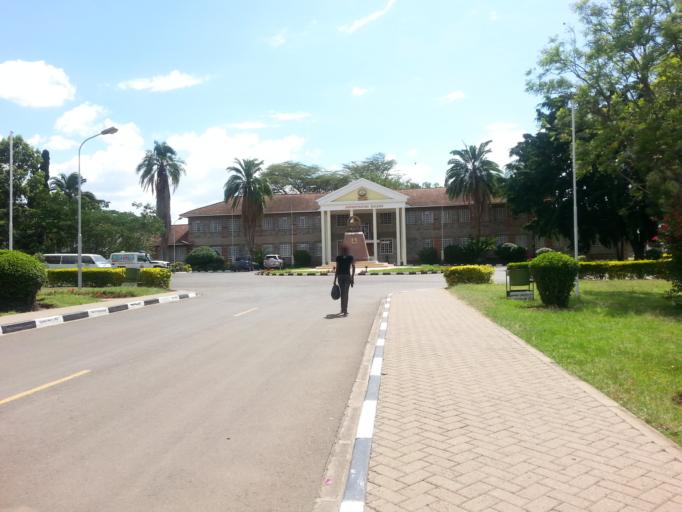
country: KE
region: Nakuru
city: Rongai
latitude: -0.1666
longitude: 35.9666
